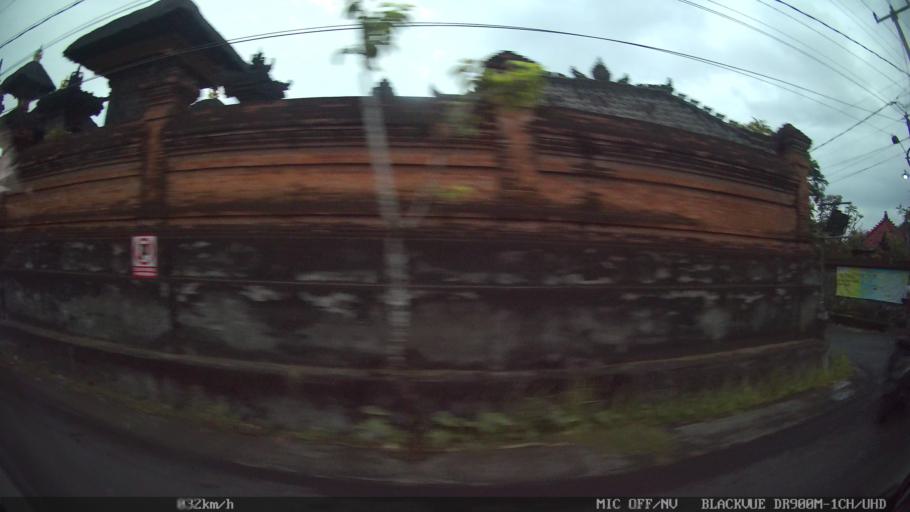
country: ID
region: Bali
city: Banjar Pasekan
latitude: -8.6178
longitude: 115.2693
